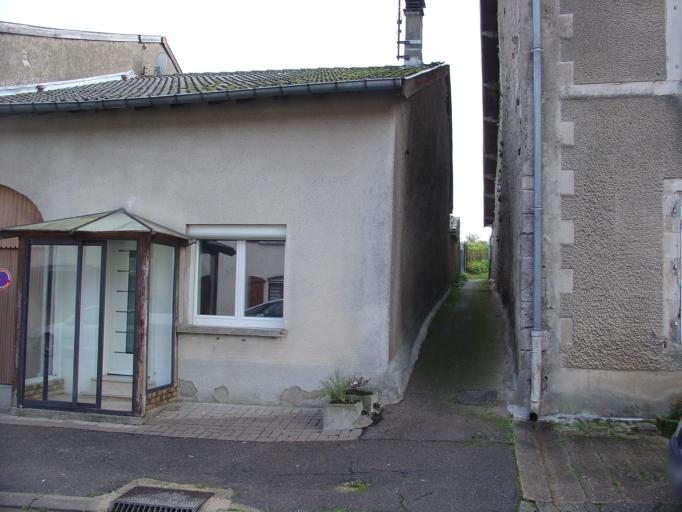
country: FR
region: Lorraine
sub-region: Departement de Meurthe-et-Moselle
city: Colombey-les-Belles
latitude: 48.5825
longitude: 5.9431
